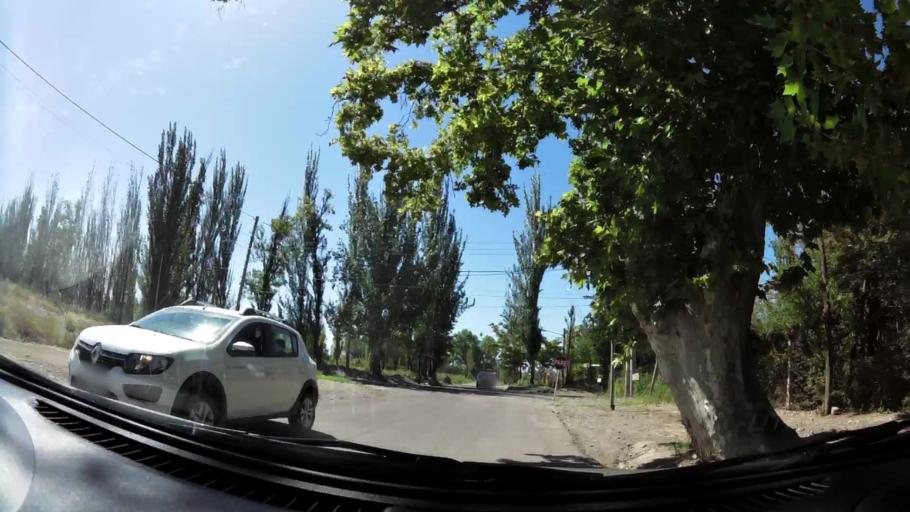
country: AR
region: Mendoza
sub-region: Departamento de Godoy Cruz
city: Godoy Cruz
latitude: -32.9858
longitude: -68.8438
